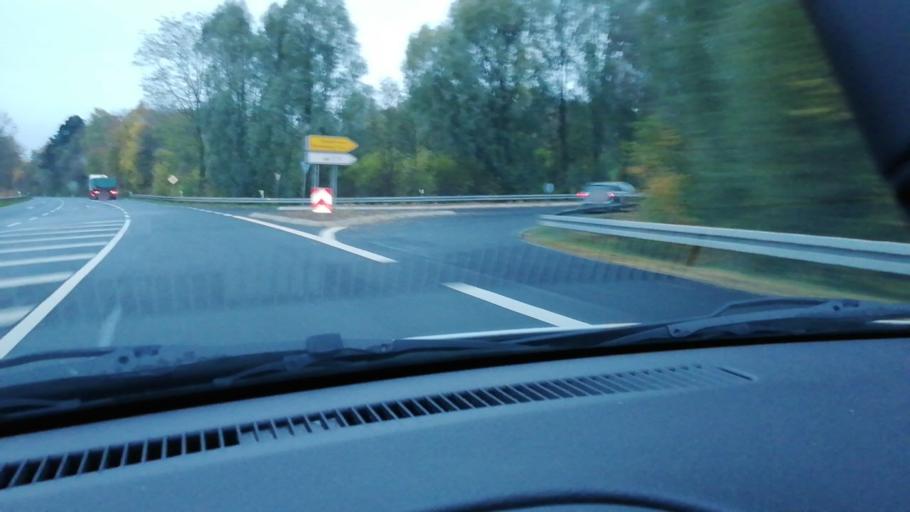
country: DE
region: Bavaria
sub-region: Regierungsbezirk Unterfranken
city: Hosbach
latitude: 50.0295
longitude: 9.2108
